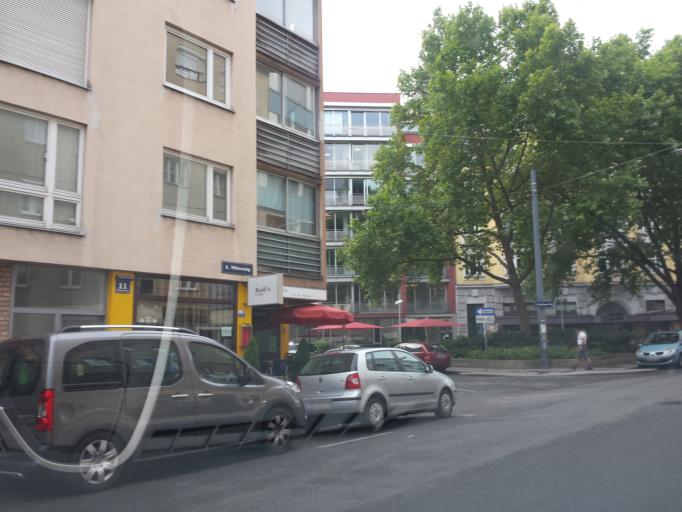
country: AT
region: Vienna
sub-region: Wien Stadt
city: Vienna
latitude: 48.1915
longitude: 16.3638
